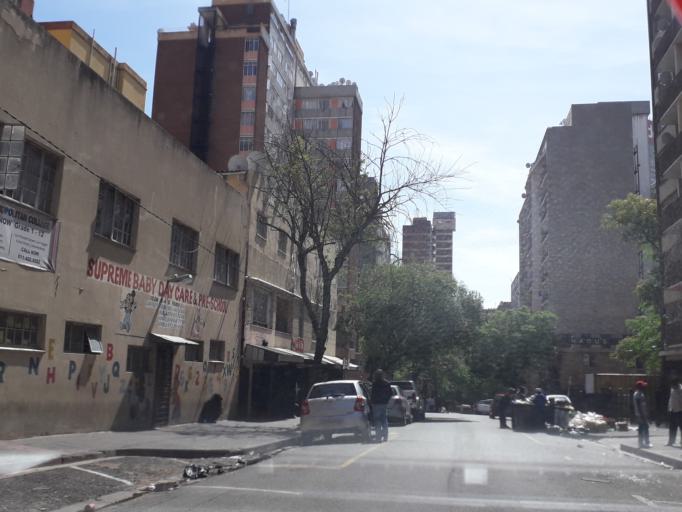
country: ZA
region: Gauteng
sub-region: City of Johannesburg Metropolitan Municipality
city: Johannesburg
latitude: -26.1906
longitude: 28.0525
